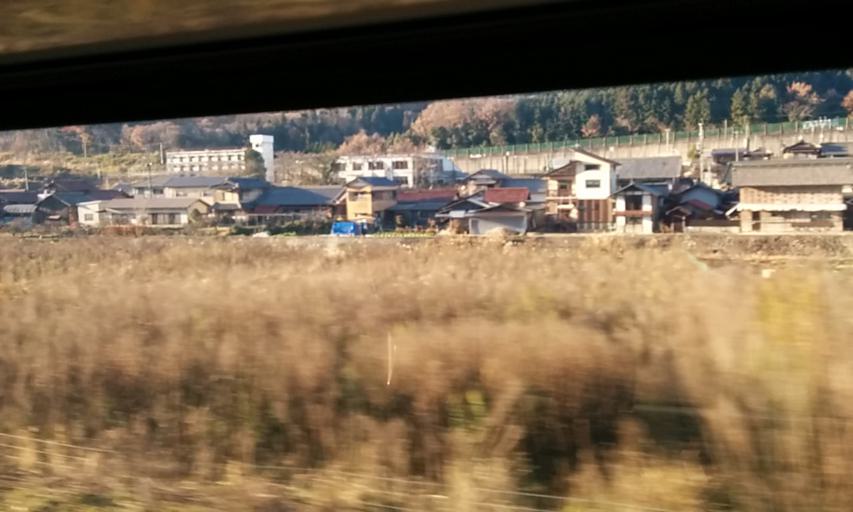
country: JP
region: Gifu
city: Mizunami
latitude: 35.4173
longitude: 137.3190
